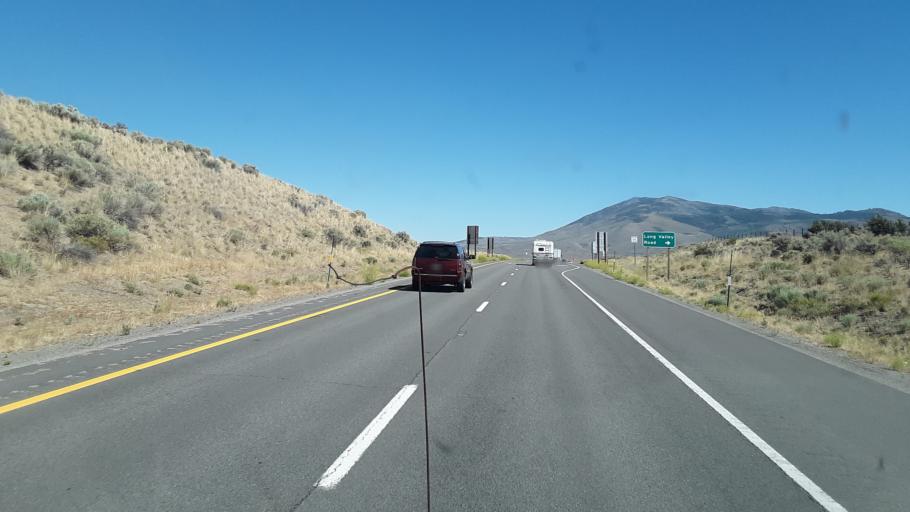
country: US
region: Nevada
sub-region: Washoe County
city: Cold Springs
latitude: 39.6763
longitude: -120.0039
